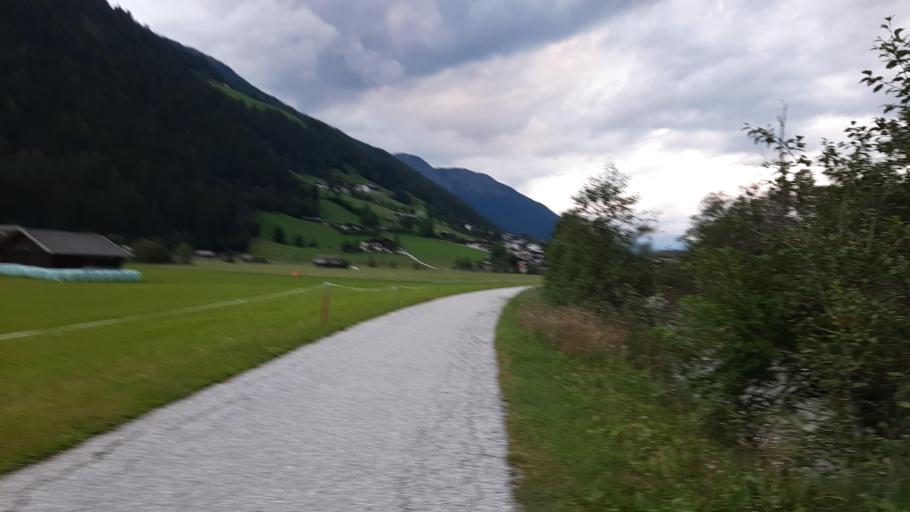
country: AT
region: Tyrol
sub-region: Politischer Bezirk Innsbruck Land
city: Neustift im Stubaital
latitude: 47.1169
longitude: 11.3220
